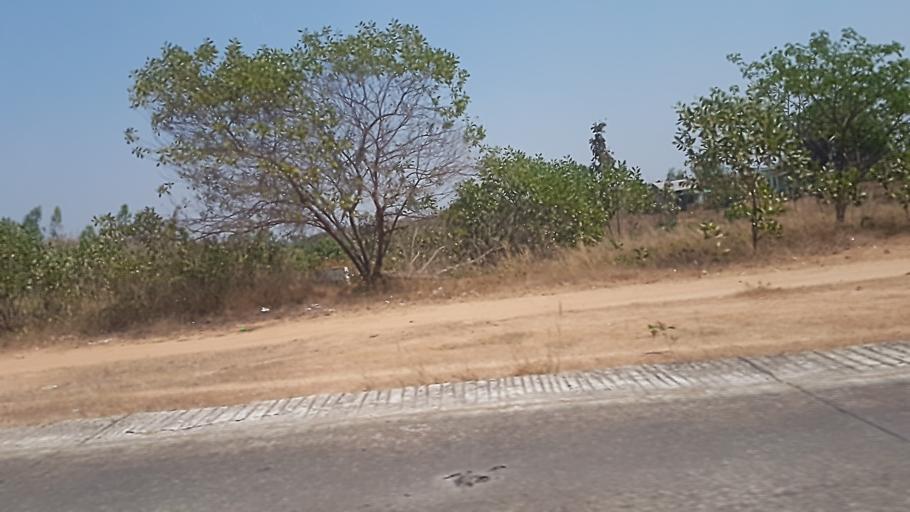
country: MM
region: Bago
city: Pyu
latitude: 18.2723
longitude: 96.4505
